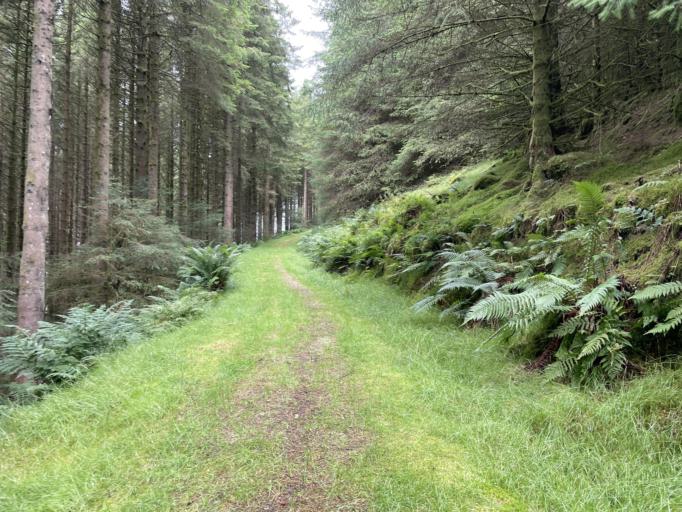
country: GB
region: Scotland
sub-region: South Ayrshire
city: Maybole
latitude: 55.1979
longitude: -4.6665
